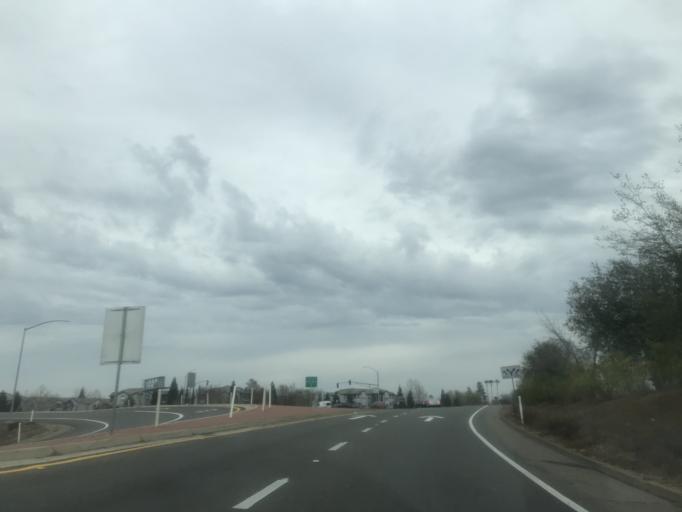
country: US
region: California
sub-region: Sacramento County
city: Rancho Cordova
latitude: 38.5773
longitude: -121.3086
